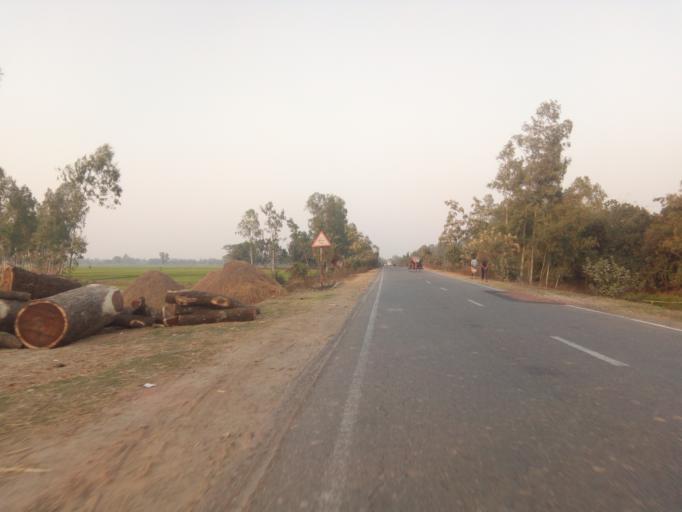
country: BD
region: Rajshahi
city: Bogra
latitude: 24.5959
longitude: 89.2376
